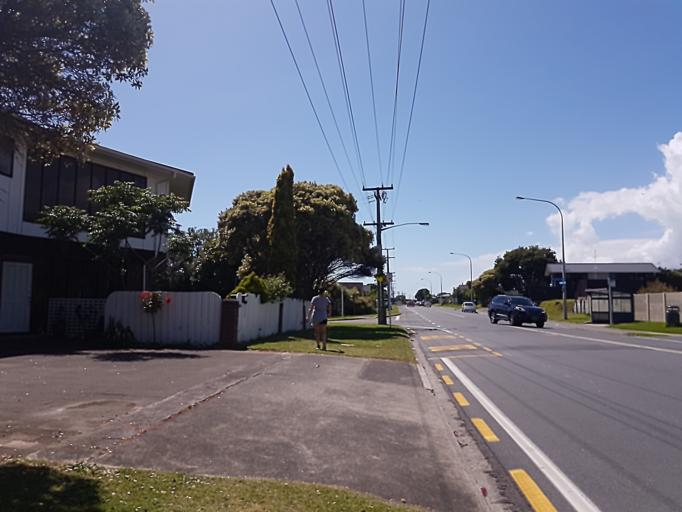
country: NZ
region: Bay of Plenty
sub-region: Western Bay of Plenty District
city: Maketu
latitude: -37.7138
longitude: 176.3327
